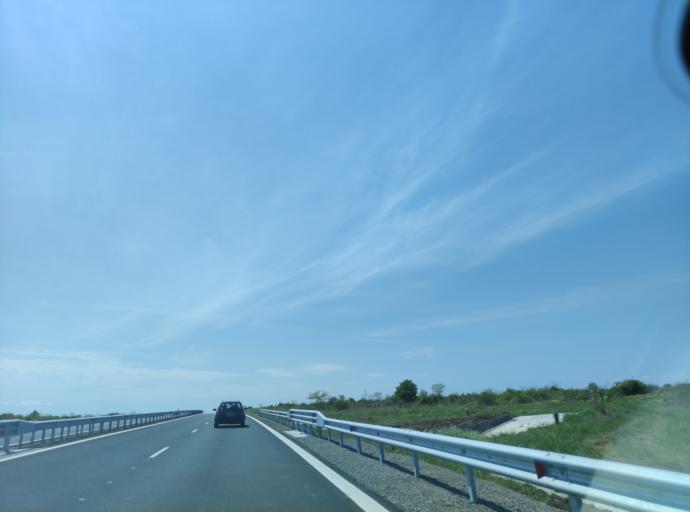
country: BG
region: Burgas
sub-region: Obshtina Pomorie
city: Pomorie
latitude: 42.5862
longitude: 27.5903
